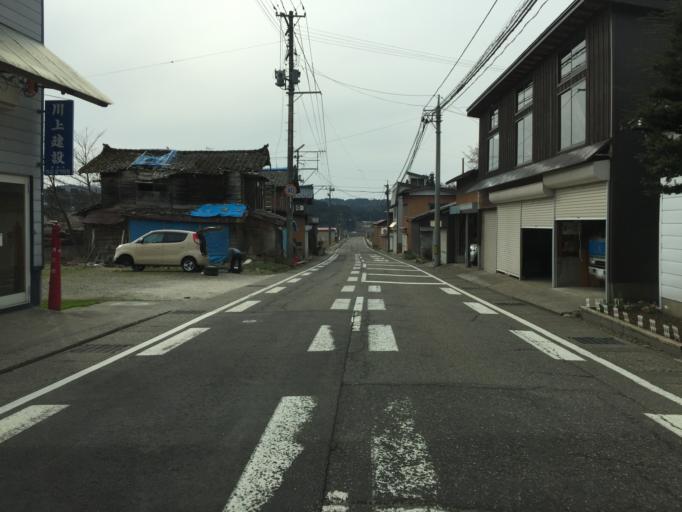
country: JP
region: Niigata
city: Tochio-honcho
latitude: 37.4447
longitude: 139.0273
